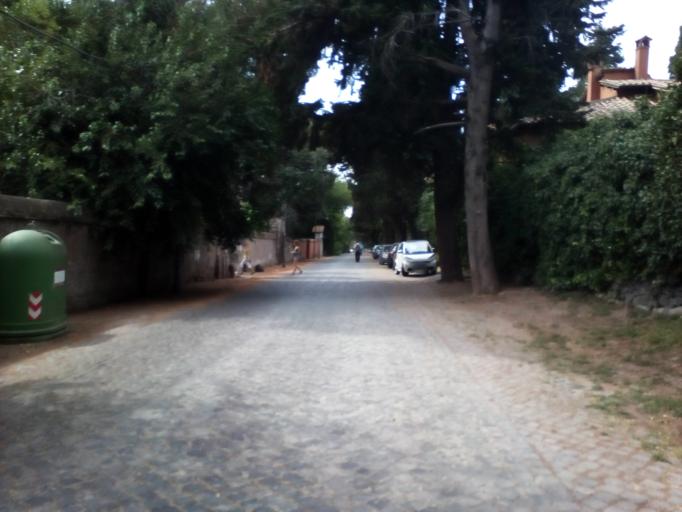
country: IT
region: Latium
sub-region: Citta metropolitana di Roma Capitale
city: Rome
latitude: 41.8473
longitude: 12.5260
